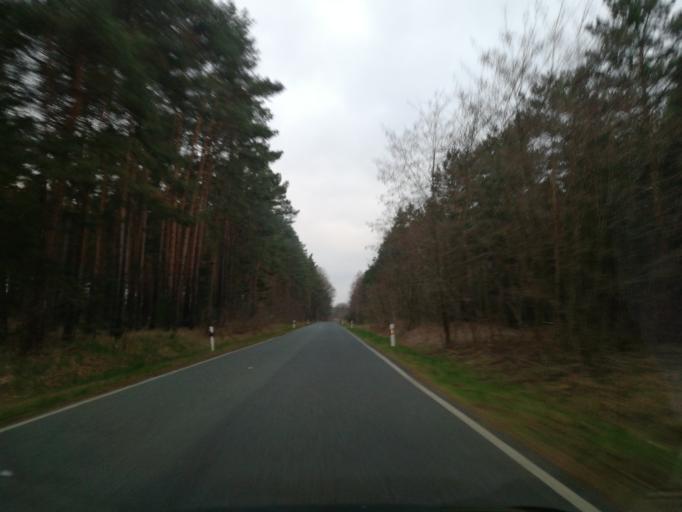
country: DE
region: Brandenburg
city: Vetschau
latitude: 51.7630
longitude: 14.0875
